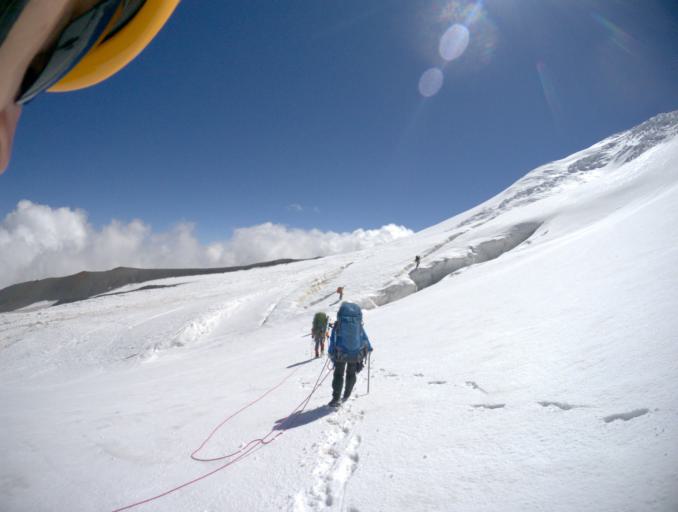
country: RU
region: Kabardino-Balkariya
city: Terskol
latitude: 43.3814
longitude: 42.4460
